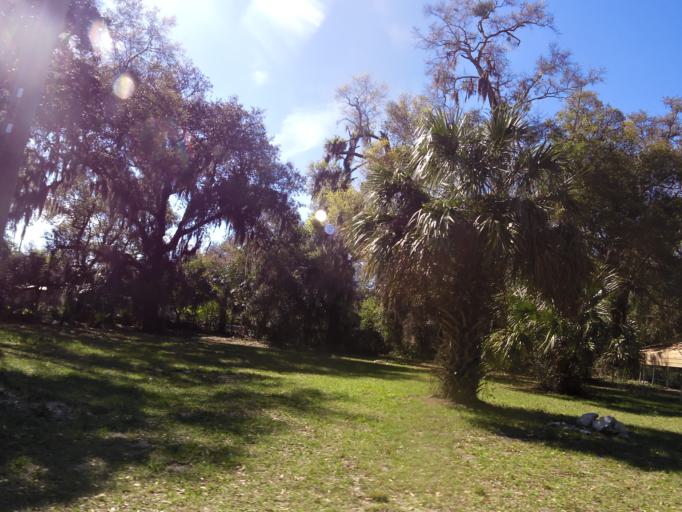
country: US
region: Florida
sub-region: Duval County
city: Jacksonville
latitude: 30.3620
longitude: -81.6462
